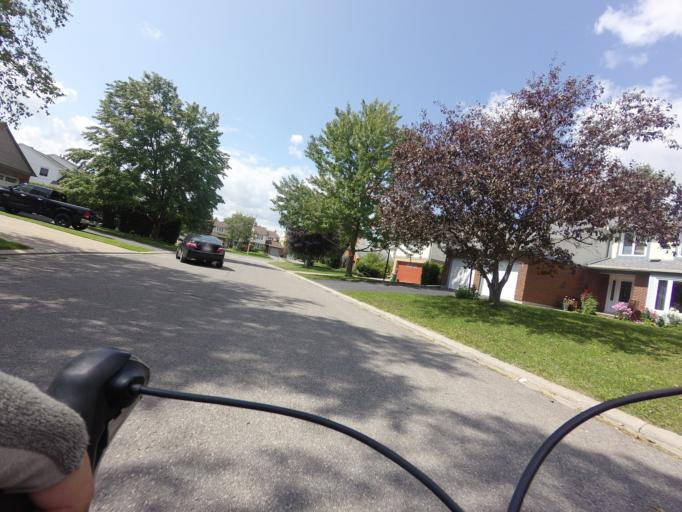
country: CA
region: Ontario
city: Bells Corners
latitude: 45.2840
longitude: -75.8640
